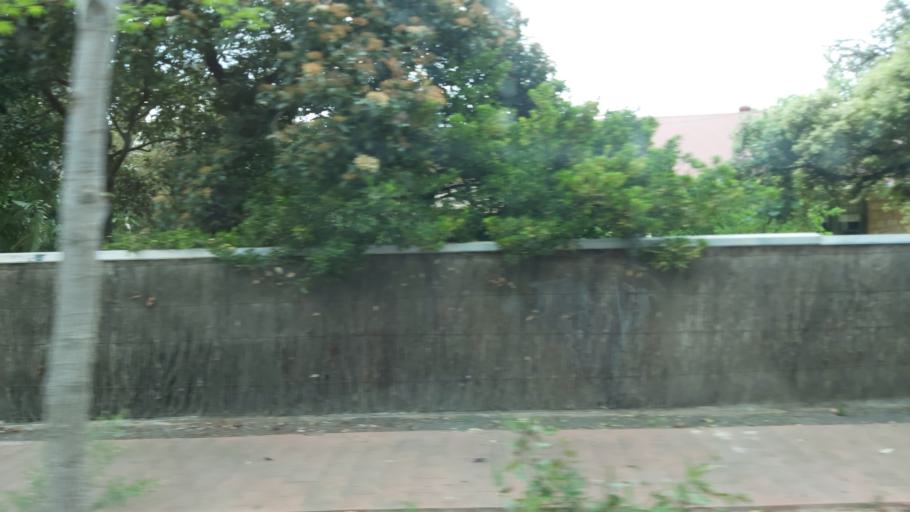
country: AU
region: South Australia
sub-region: Burnside
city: Glenunga
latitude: -34.9585
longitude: 138.6362
